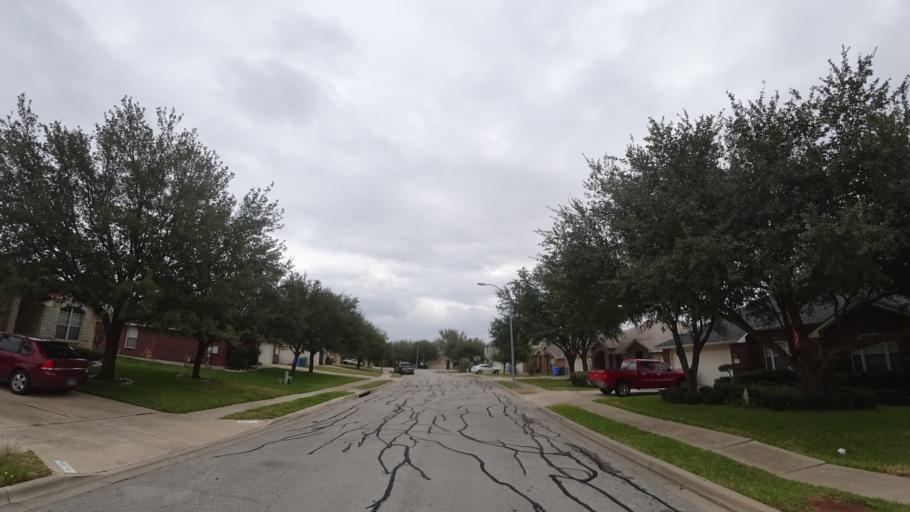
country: US
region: Texas
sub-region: Travis County
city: Pflugerville
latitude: 30.4353
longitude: -97.6055
